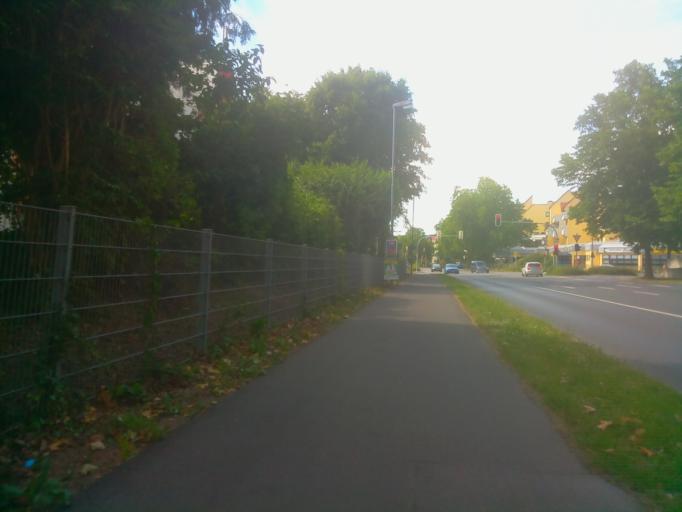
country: DE
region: Baden-Wuerttemberg
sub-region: Karlsruhe Region
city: Dossenheim
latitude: 49.4446
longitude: 8.6754
